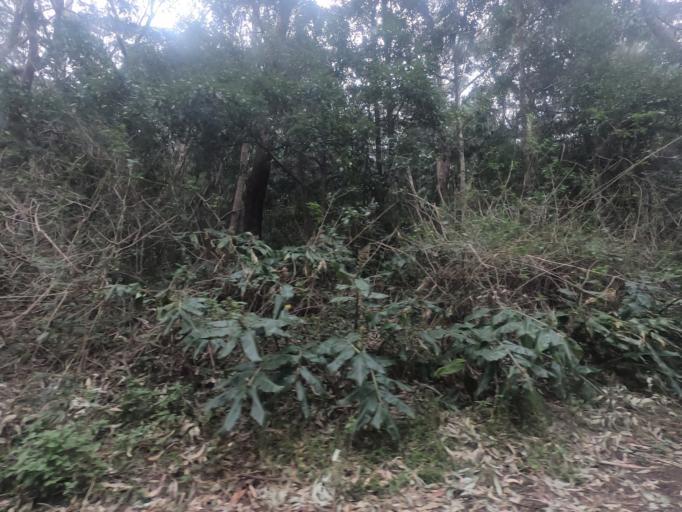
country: AU
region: New South Wales
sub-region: Wollongong
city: Bulli
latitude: -34.2985
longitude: 150.9311
